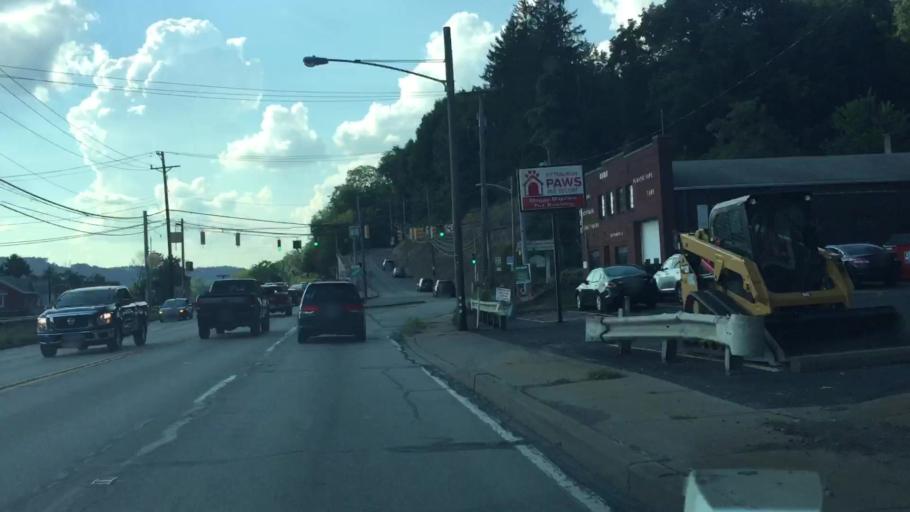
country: US
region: Pennsylvania
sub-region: Allegheny County
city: Coraopolis
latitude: 40.5246
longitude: -80.1501
